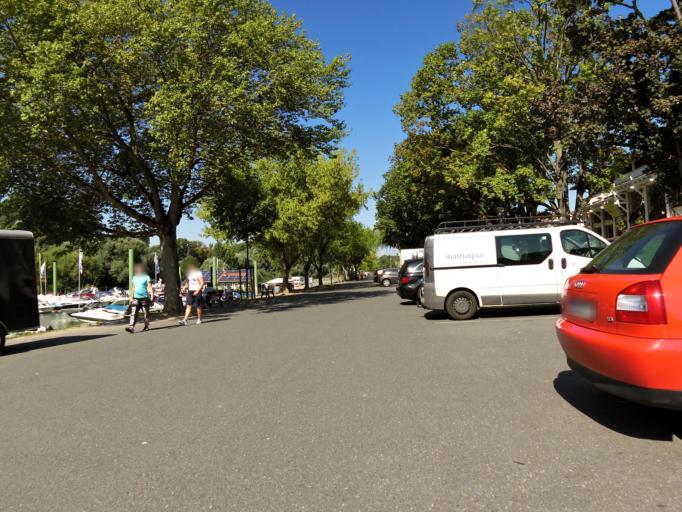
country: DE
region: Hesse
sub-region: Regierungsbezirk Darmstadt
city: Ginsheim-Gustavsburg
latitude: 49.9626
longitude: 8.3458
